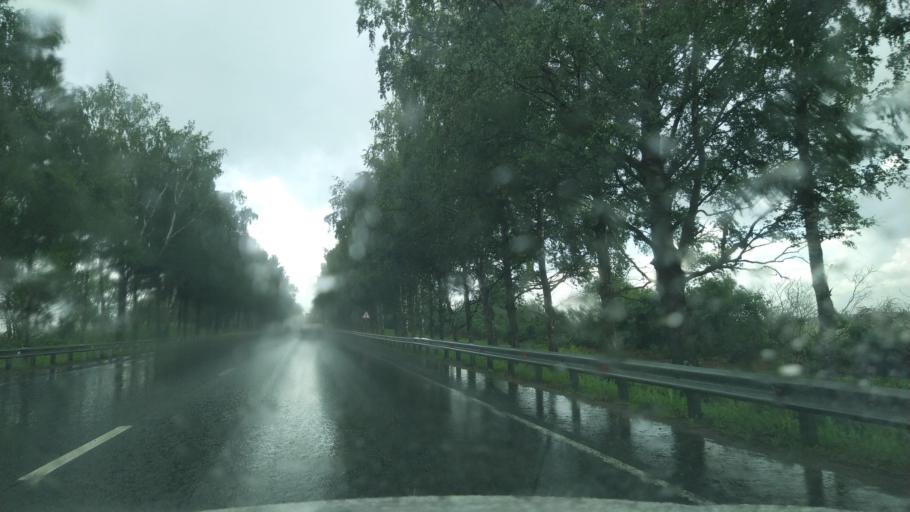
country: RU
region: Leningrad
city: Mariyenburg
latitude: 59.4990
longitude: 30.0419
